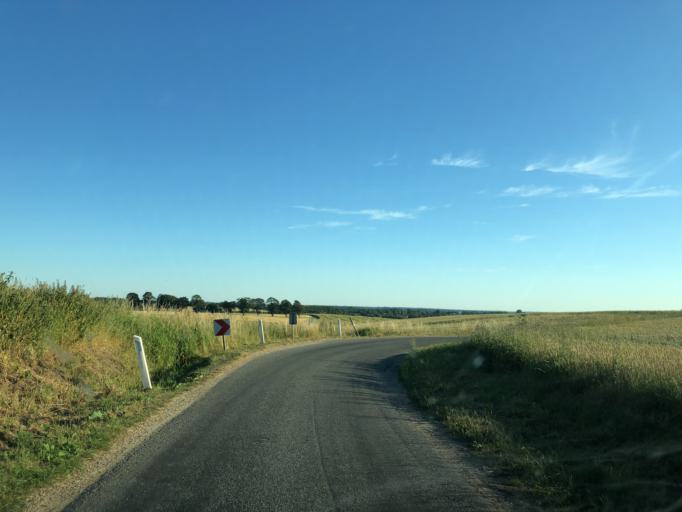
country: DK
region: Central Jutland
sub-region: Horsens Kommune
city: Horsens
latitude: 55.9054
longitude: 9.8665
